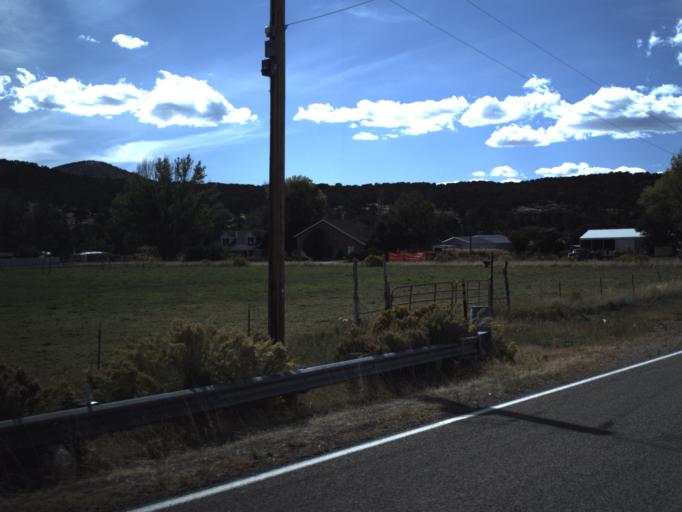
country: US
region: Utah
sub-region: Washington County
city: Enterprise
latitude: 37.5735
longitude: -113.7293
